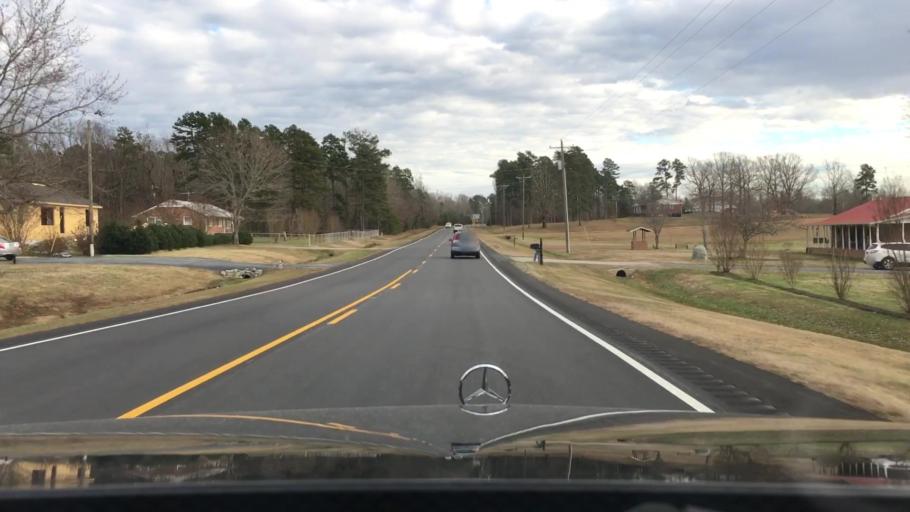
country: US
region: North Carolina
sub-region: Caswell County
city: Yanceyville
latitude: 36.2736
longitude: -79.2037
